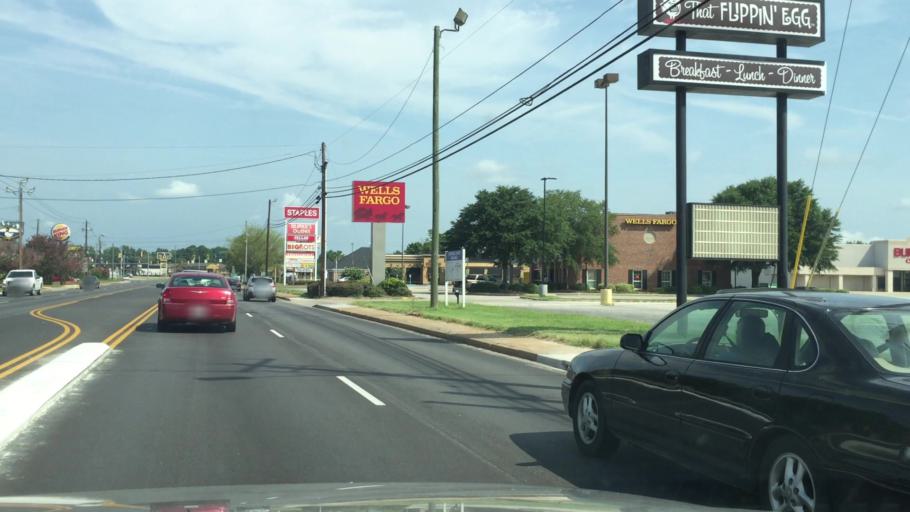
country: US
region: South Carolina
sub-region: Sumter County
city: Sumter
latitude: 33.9523
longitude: -80.3777
